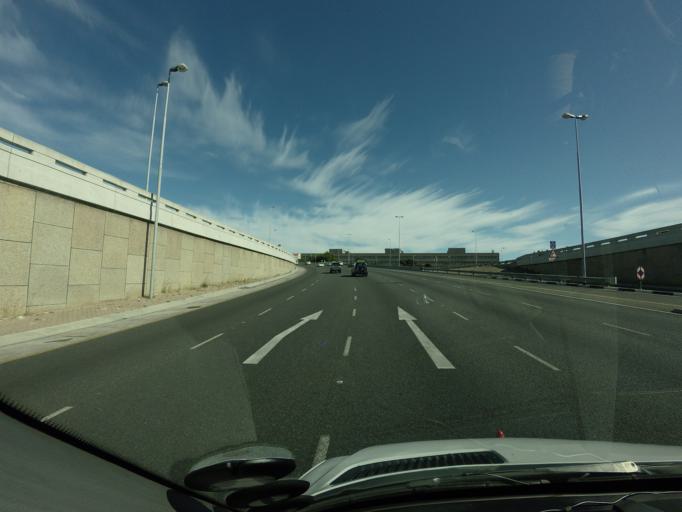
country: ZA
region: Western Cape
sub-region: City of Cape Town
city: Rosebank
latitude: -33.9448
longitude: 18.4654
